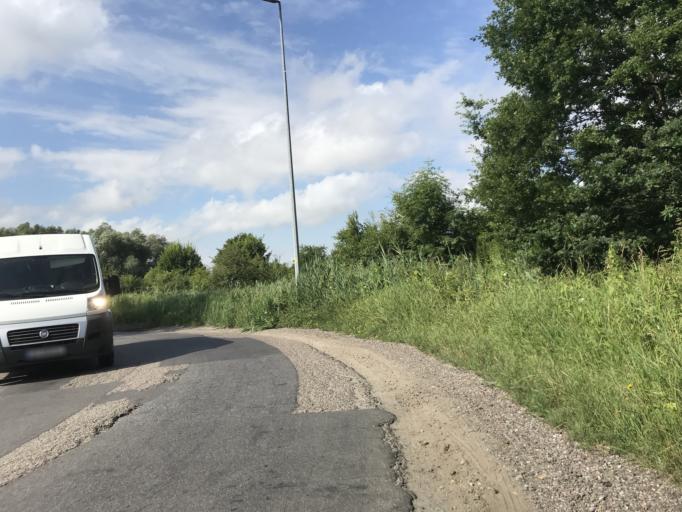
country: PL
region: Pomeranian Voivodeship
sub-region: Gdansk
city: Gdansk
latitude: 54.3402
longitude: 18.6662
